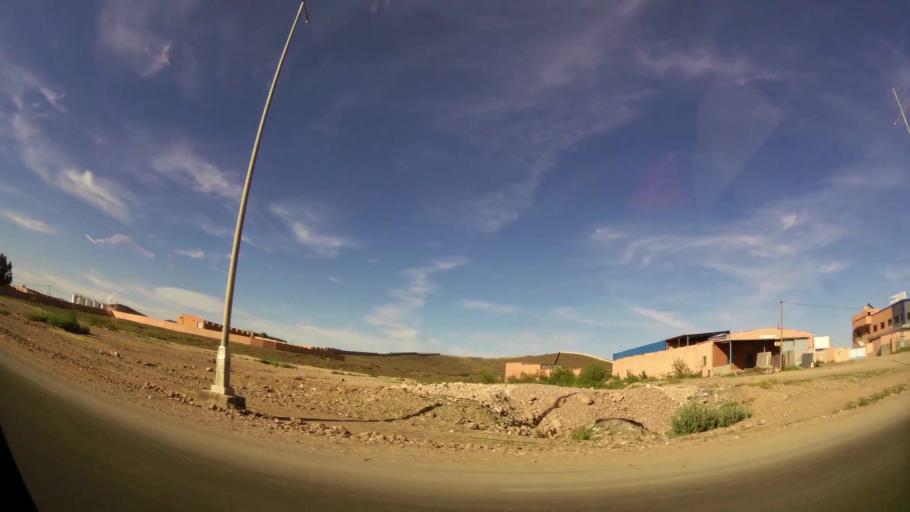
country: MA
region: Marrakech-Tensift-Al Haouz
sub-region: Marrakech
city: Marrakesh
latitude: 31.7090
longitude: -8.0660
